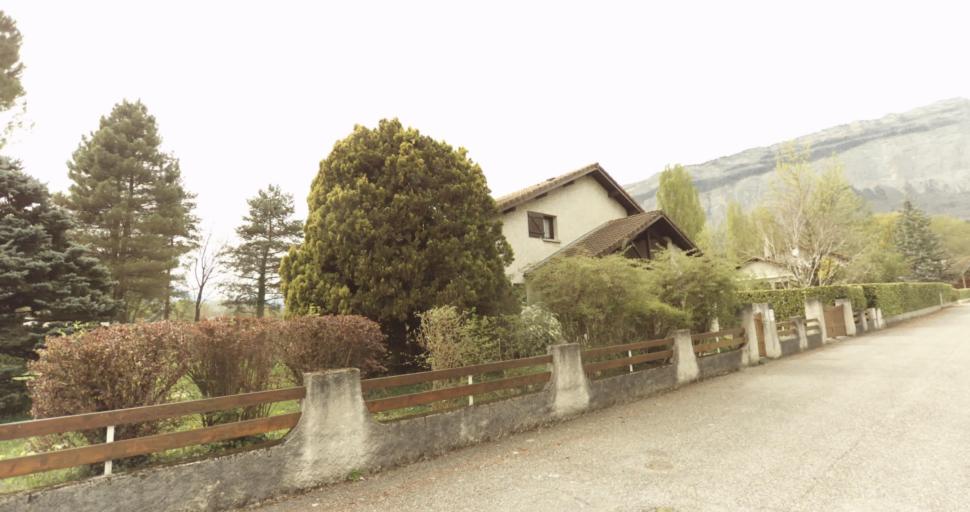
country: FR
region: Rhone-Alpes
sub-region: Departement de l'Isere
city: Montbonnot-Saint-Martin
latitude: 45.2206
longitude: 5.8083
